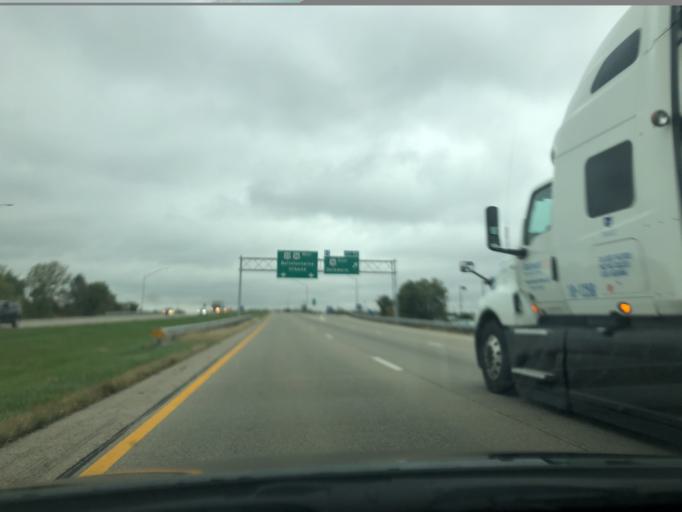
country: US
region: Ohio
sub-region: Union County
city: Marysville
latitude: 40.2357
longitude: -83.3424
